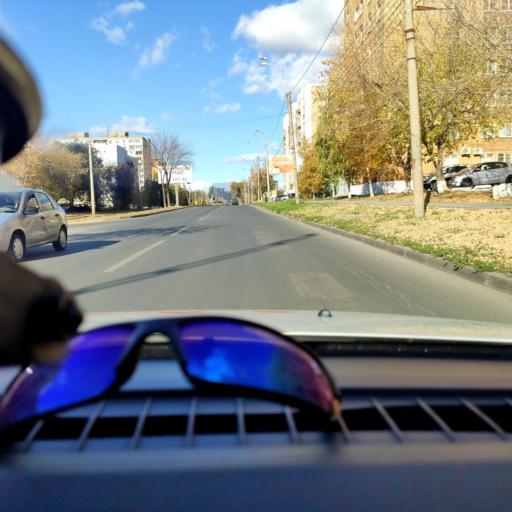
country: RU
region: Samara
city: Samara
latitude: 53.1983
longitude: 50.1552
